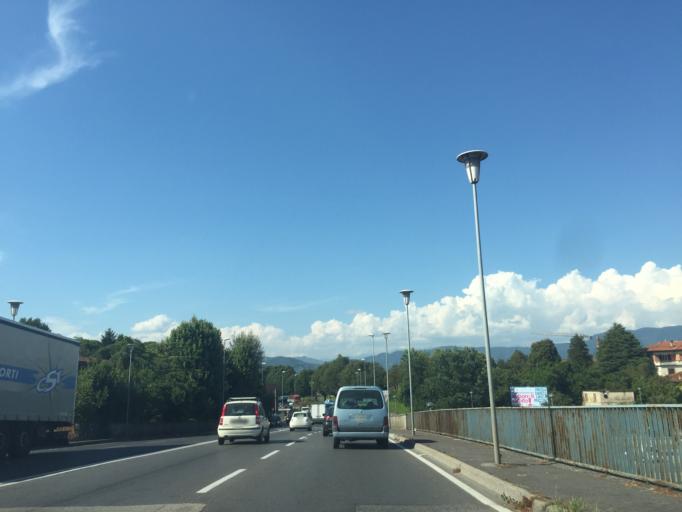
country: IT
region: Tuscany
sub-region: Provincia di Lucca
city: Lucca
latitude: 43.8379
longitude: 10.4951
